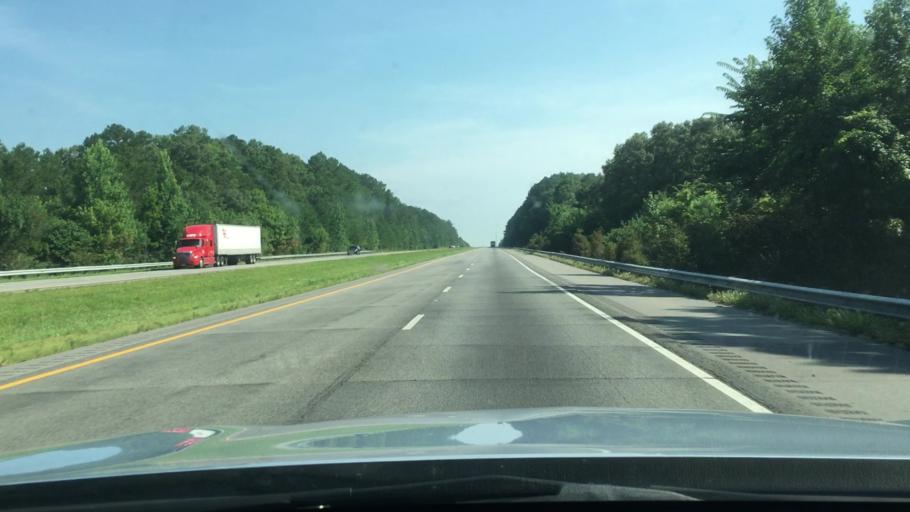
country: US
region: Alabama
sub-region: DeKalb County
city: Fort Payne
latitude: 34.5160
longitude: -85.6917
